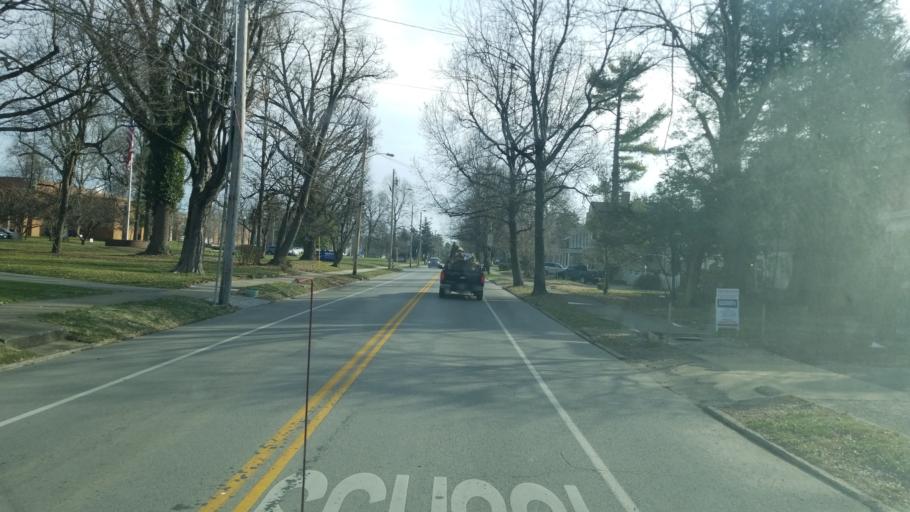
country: US
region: Kentucky
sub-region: Boyle County
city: Danville
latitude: 37.6488
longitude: -84.7692
